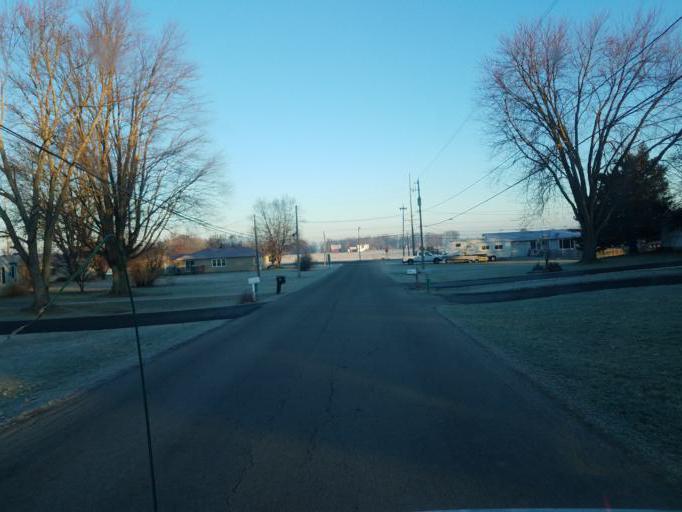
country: US
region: Ohio
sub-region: Marion County
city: Marion
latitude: 40.5630
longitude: -83.0910
